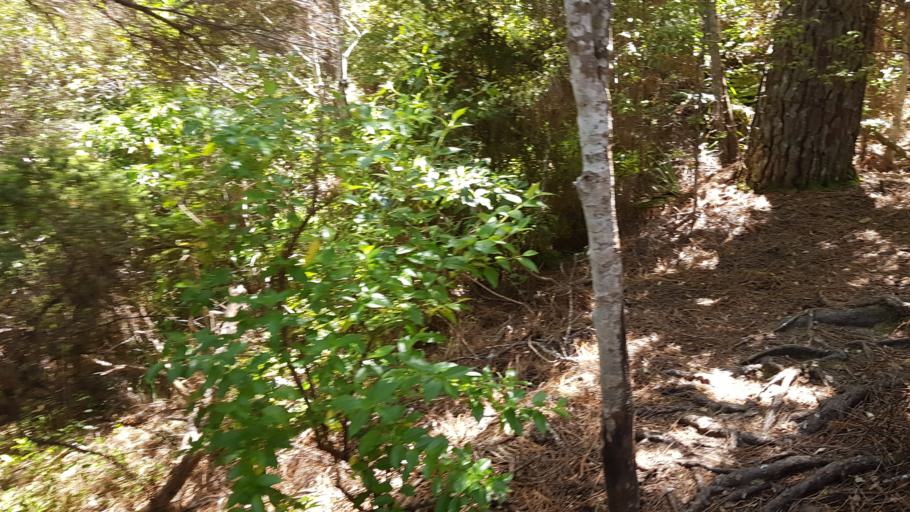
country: NZ
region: Auckland
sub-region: Auckland
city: North Shore
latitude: -36.8249
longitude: 174.7109
